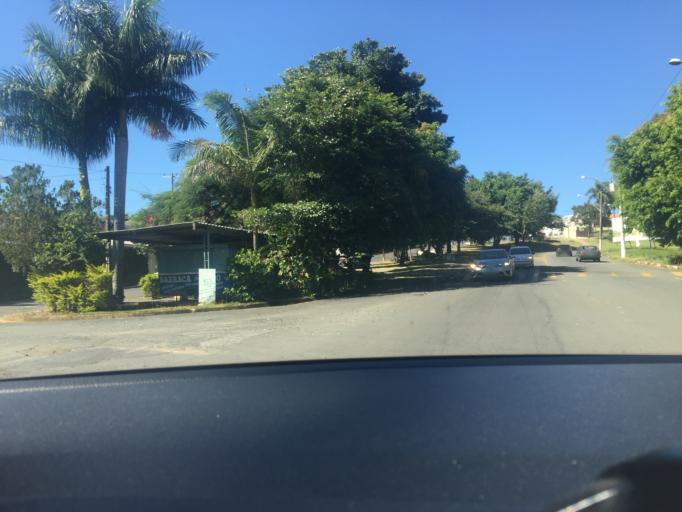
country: BR
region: Sao Paulo
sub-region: Santo Antonio Do Jardim
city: Espirito Santo do Pinhal
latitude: -22.1805
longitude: -46.7445
